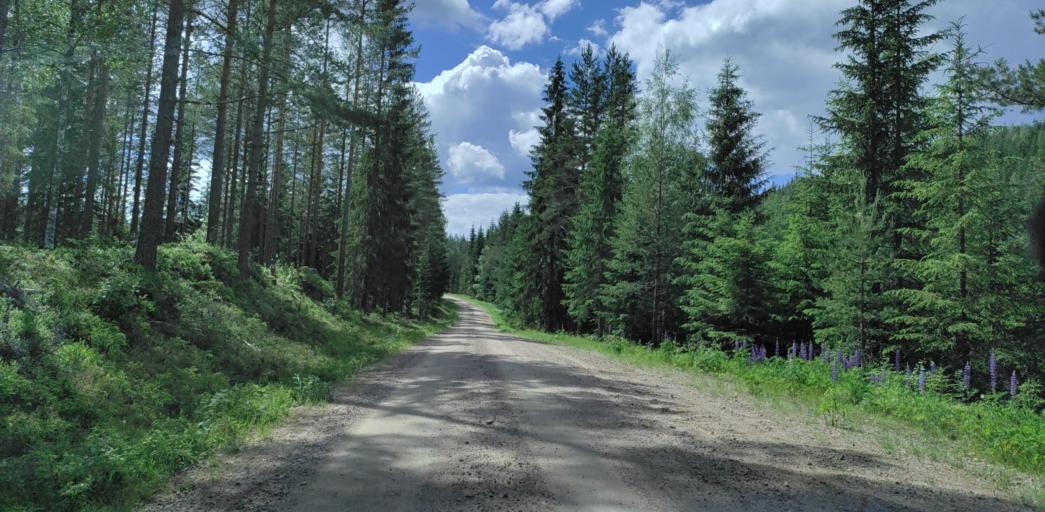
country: SE
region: Vaermland
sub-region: Hagfors Kommun
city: Ekshaerad
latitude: 60.1019
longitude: 13.3533
